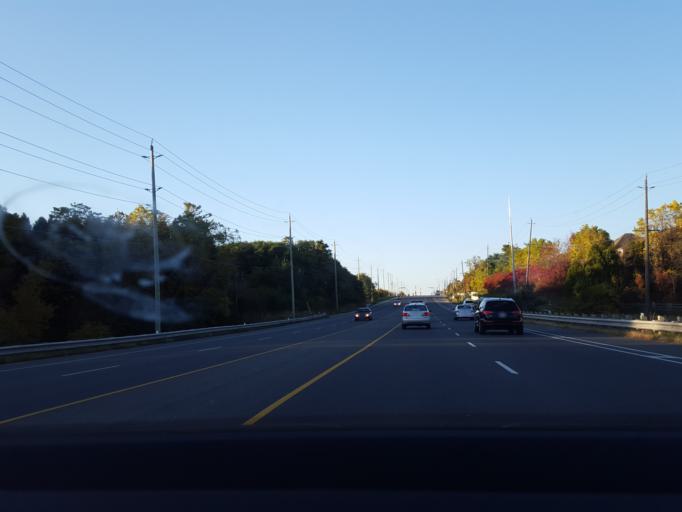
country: CA
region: Ontario
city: Newmarket
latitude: 44.0222
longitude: -79.4728
